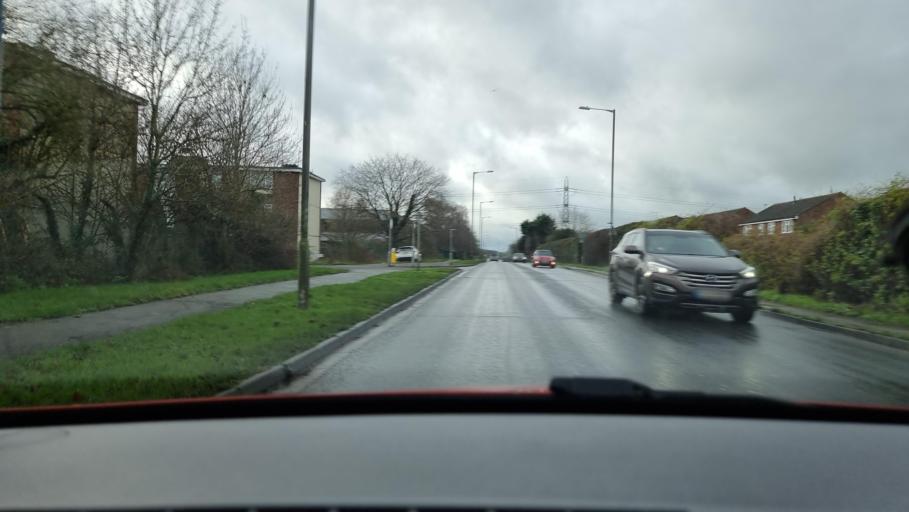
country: GB
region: England
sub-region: Buckinghamshire
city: Aylesbury
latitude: 51.8255
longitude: -0.8395
